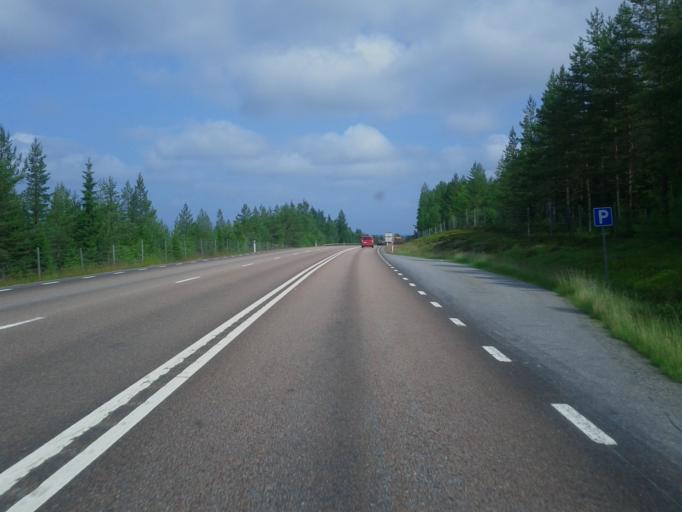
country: SE
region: Vaesterbotten
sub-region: Skelleftea Kommun
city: Burea
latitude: 64.4506
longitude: 21.2842
